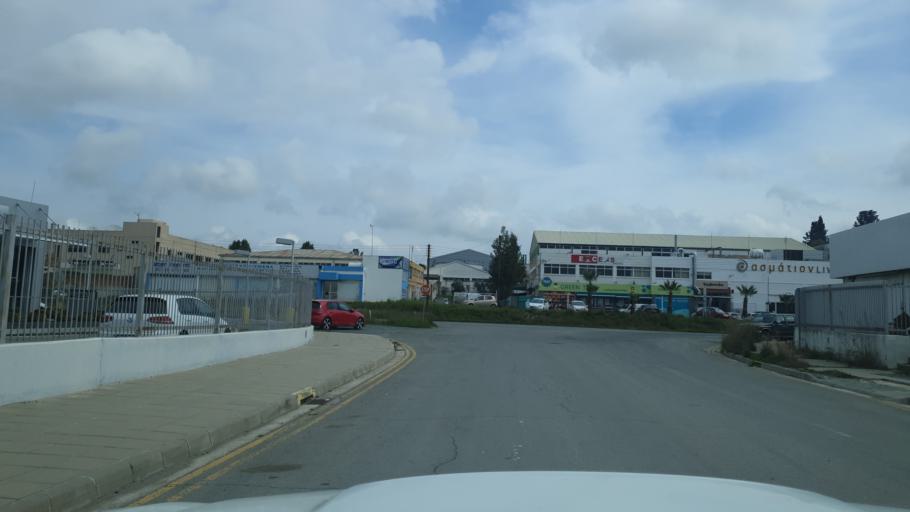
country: CY
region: Lefkosia
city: Geri
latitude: 35.0917
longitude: 33.3786
